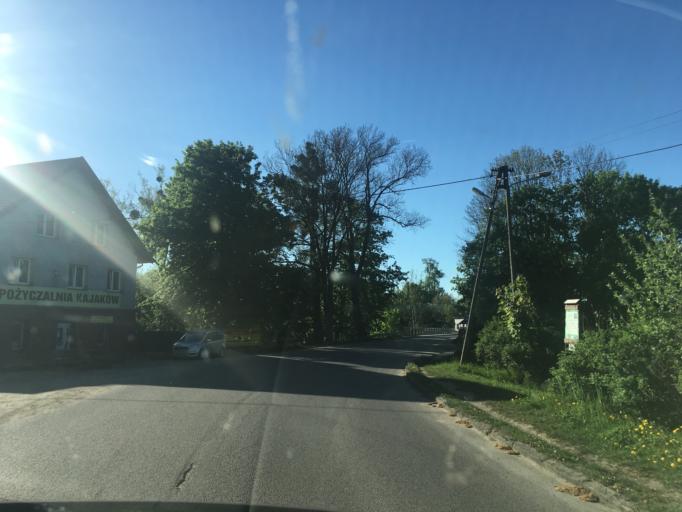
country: PL
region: Warmian-Masurian Voivodeship
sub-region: Powiat piski
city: Ruciane-Nida
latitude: 53.6874
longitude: 21.4999
